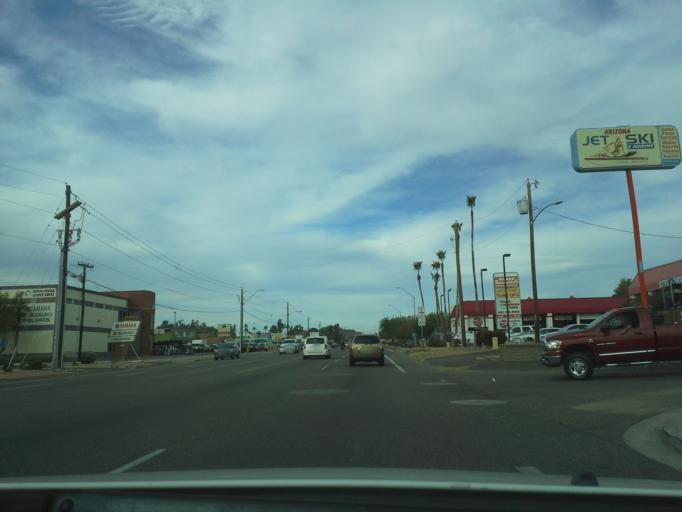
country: US
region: Arizona
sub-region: Maricopa County
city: Paradise Valley
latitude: 33.6417
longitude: -112.0308
